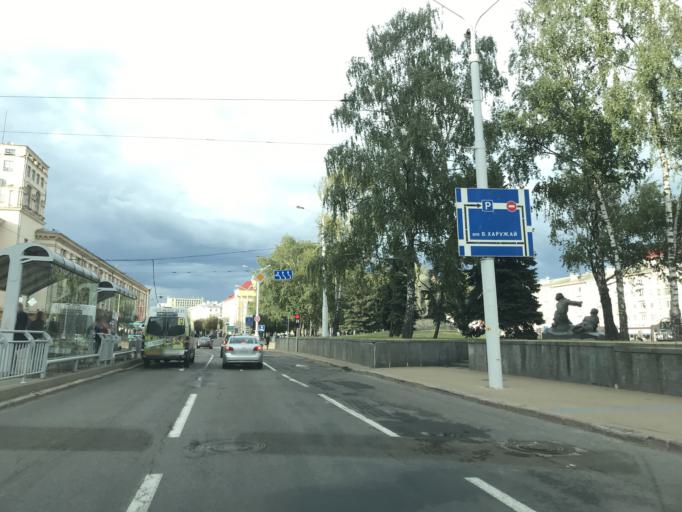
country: BY
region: Minsk
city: Minsk
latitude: 53.9154
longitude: 27.5818
